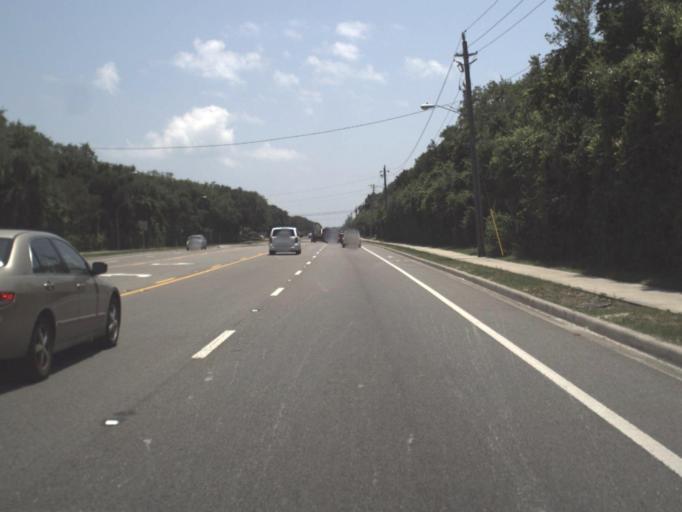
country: US
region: Florida
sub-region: Saint Johns County
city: Saint Augustine Beach
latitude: 29.8755
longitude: -81.2854
